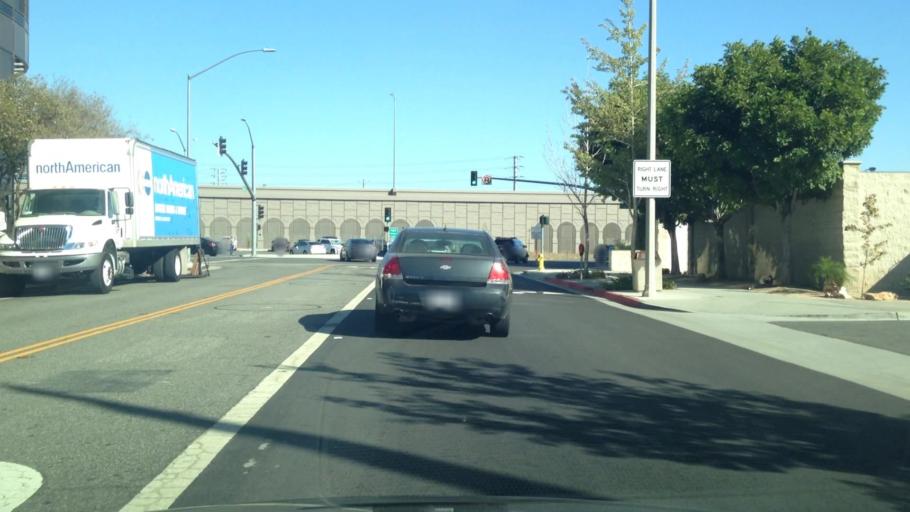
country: US
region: California
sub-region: Riverside County
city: Riverside
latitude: 33.9786
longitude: -117.3730
